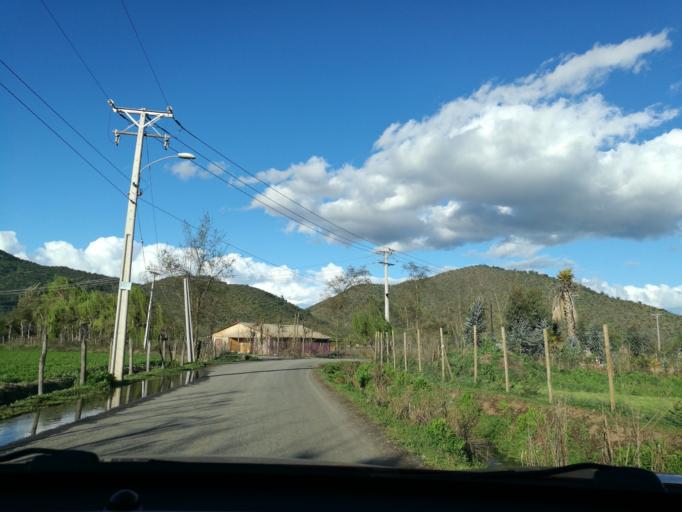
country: CL
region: O'Higgins
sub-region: Provincia de Cachapoal
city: Graneros
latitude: -34.0935
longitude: -70.8224
